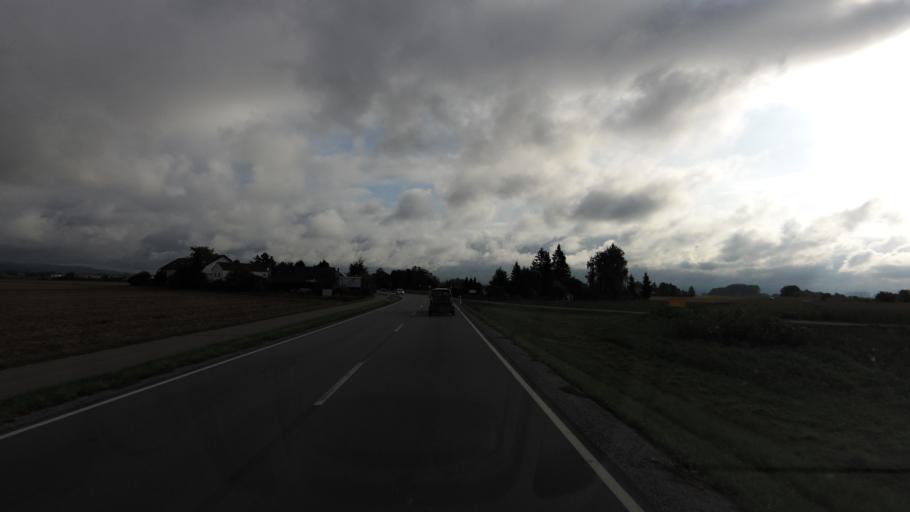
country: DE
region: Bavaria
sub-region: Lower Bavaria
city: Parkstetten
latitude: 48.9021
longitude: 12.5866
